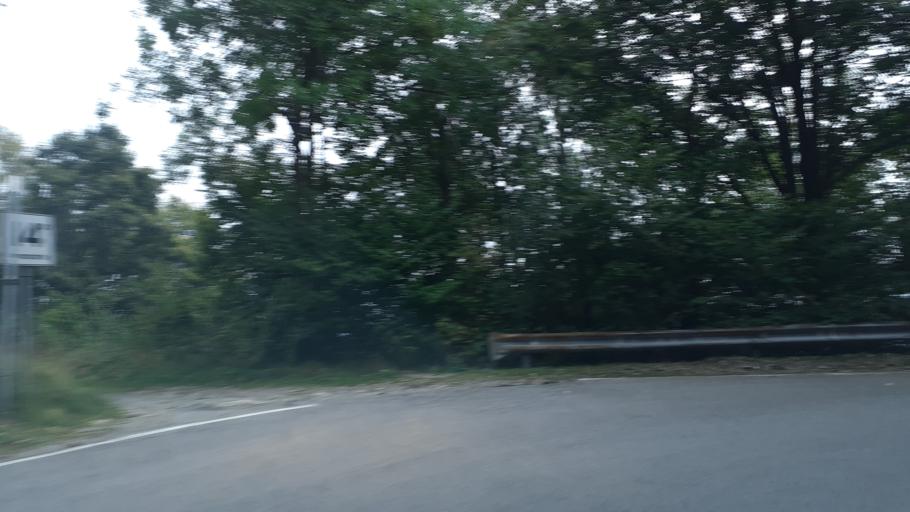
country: IT
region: Lombardy
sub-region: Provincia di Lecco
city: Ballabio
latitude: 45.8991
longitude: 9.4062
